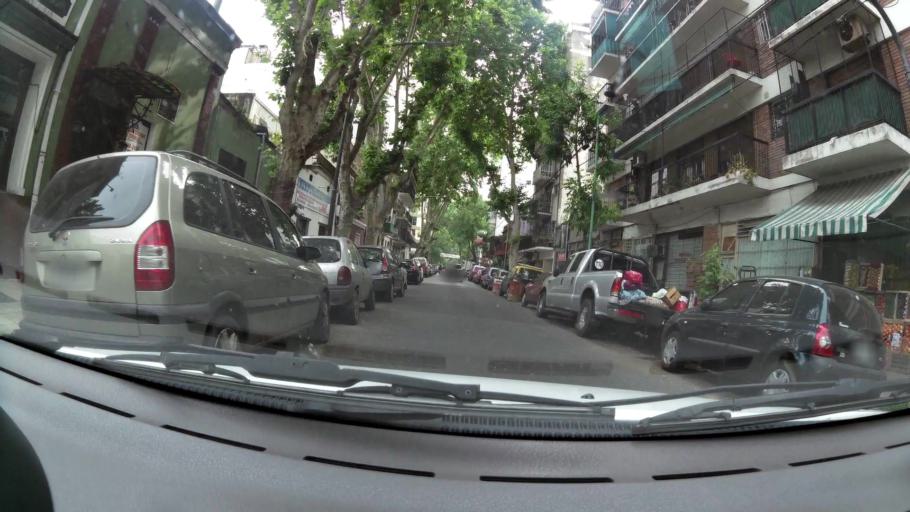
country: AR
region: Buenos Aires F.D.
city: Colegiales
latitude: -34.5581
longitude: -58.4572
